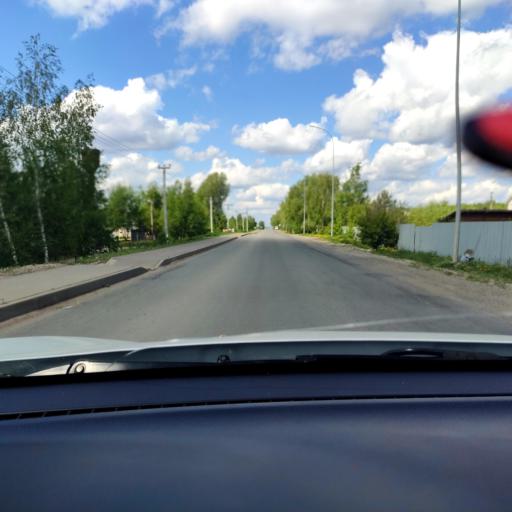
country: RU
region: Tatarstan
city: Stolbishchi
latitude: 55.6979
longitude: 49.1886
